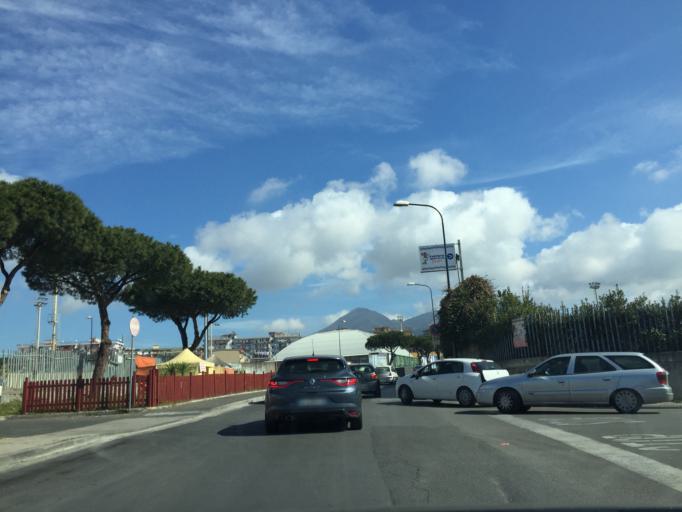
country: IT
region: Campania
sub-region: Provincia di Napoli
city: Portici
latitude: 40.8249
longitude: 14.3315
